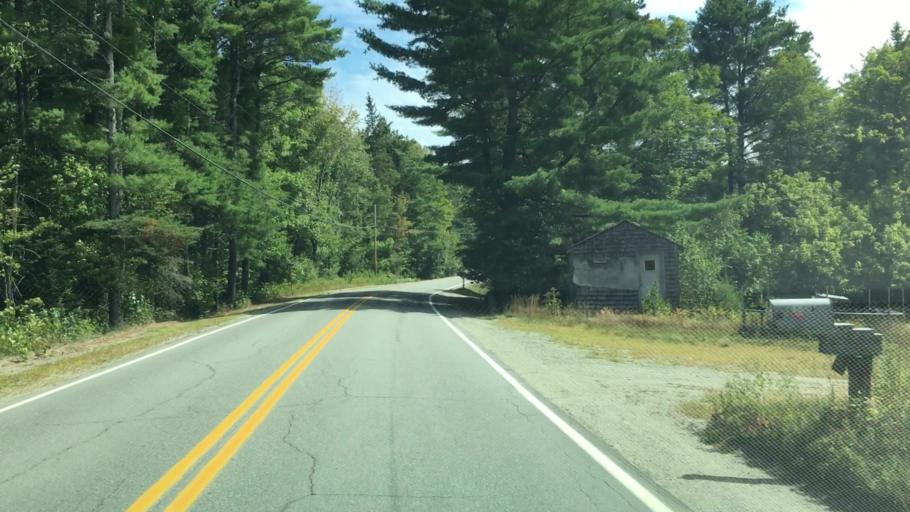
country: US
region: Maine
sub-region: Penobscot County
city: Holden
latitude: 44.7949
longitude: -68.5300
